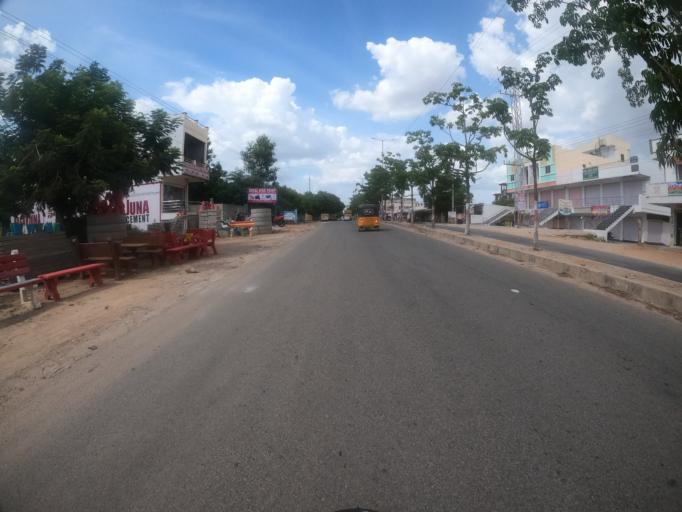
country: IN
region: Telangana
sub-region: Rangareddi
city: Sriramnagar
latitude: 17.3260
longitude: 78.2697
